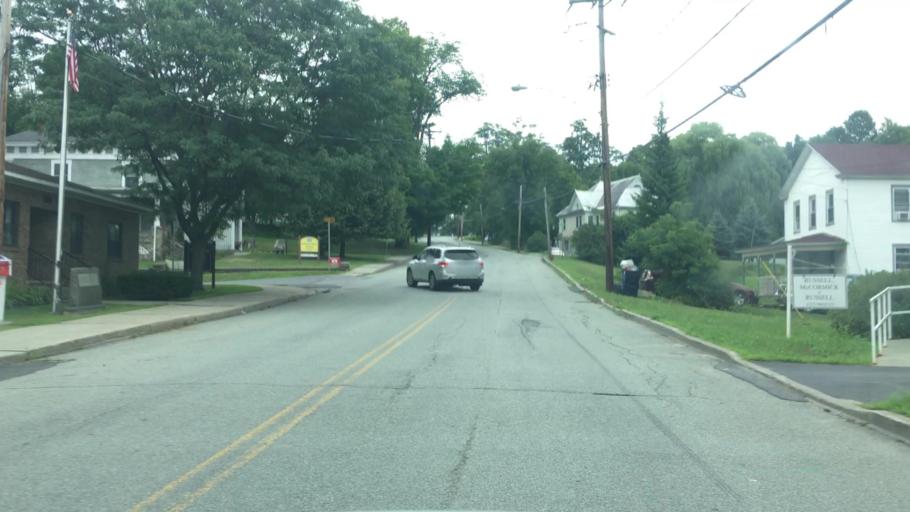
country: US
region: New York
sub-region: Essex County
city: Keeseville
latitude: 44.5031
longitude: -73.4796
